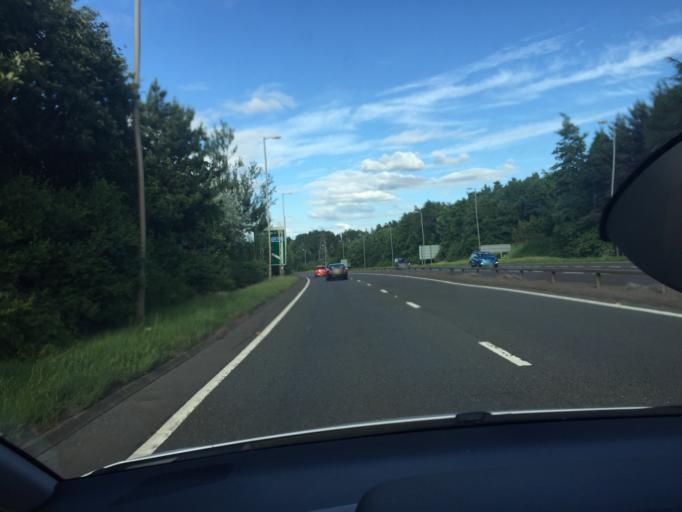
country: GB
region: Scotland
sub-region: South Lanarkshire
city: High Blantyre
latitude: 55.7824
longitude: -4.0989
